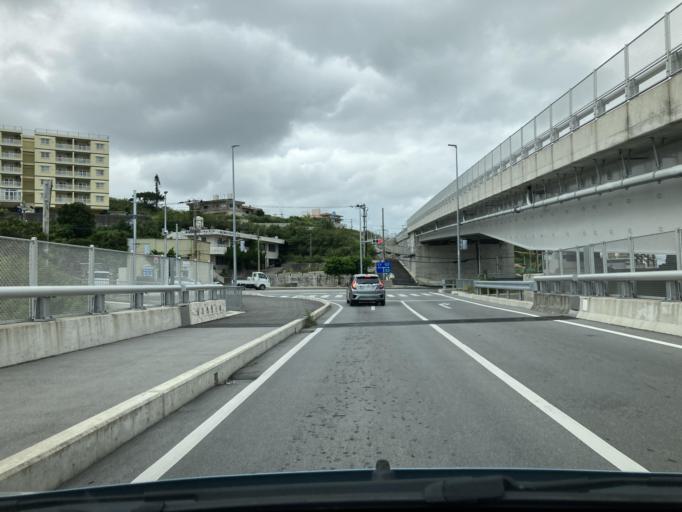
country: JP
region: Okinawa
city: Ginowan
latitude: 26.2418
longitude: 127.7408
